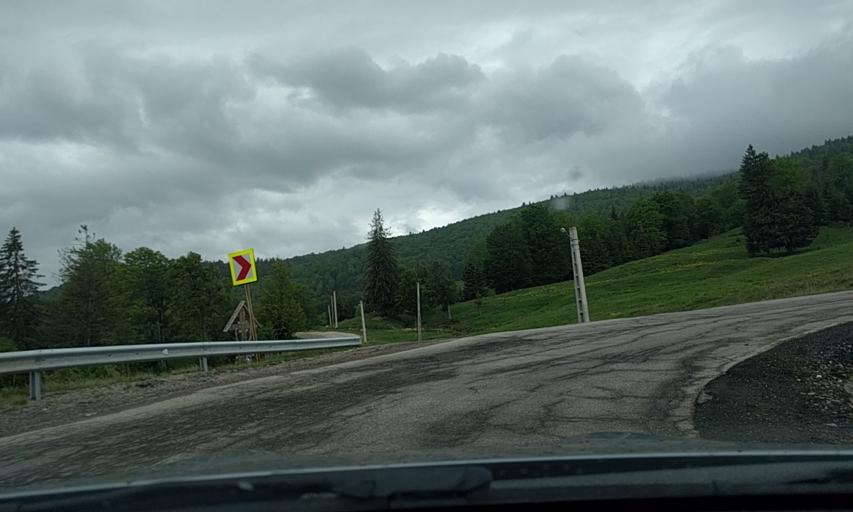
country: RO
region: Prahova
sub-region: Oras Sinaia
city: Sinaia
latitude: 45.3050
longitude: 25.5170
